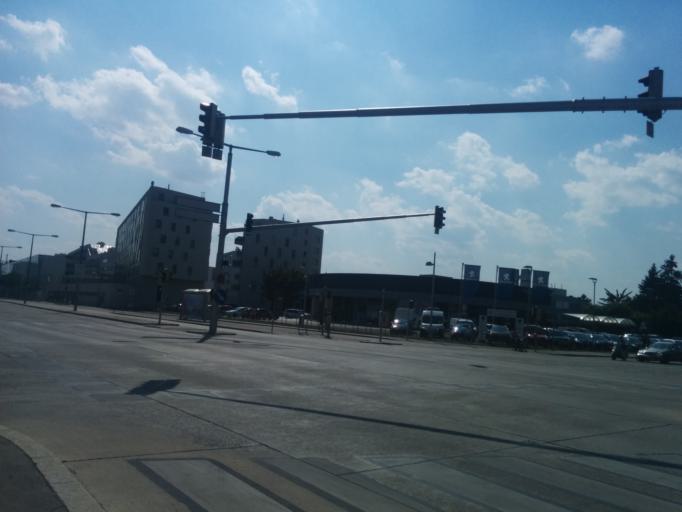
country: AT
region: Lower Austria
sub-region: Politischer Bezirk Wien-Umgebung
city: Gerasdorf bei Wien
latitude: 48.2538
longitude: 16.4466
